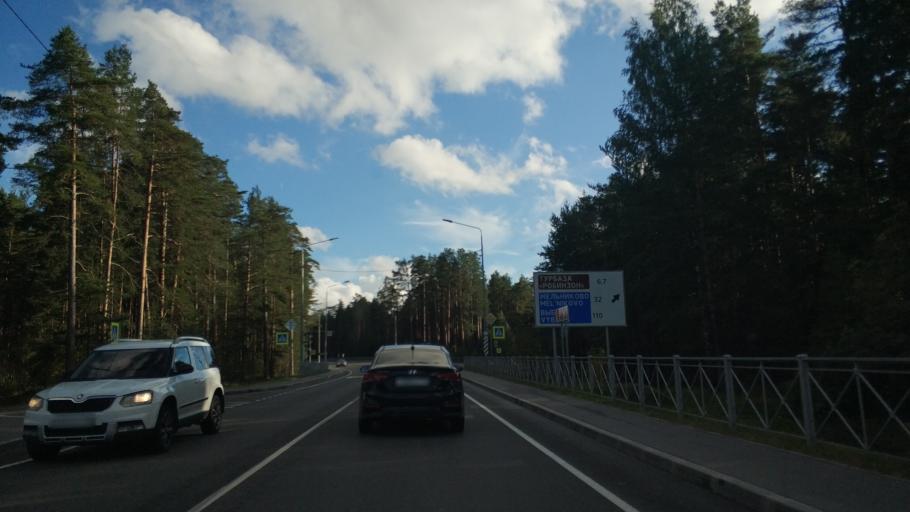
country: RU
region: Leningrad
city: Priozersk
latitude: 60.9980
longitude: 30.1824
